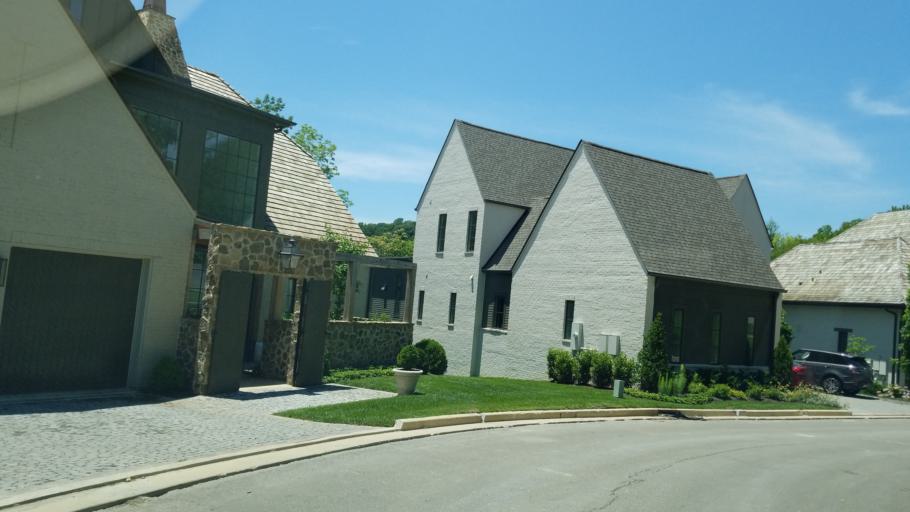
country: US
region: Tennessee
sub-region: Williamson County
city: Brentwood
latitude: 36.0512
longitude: -86.8120
